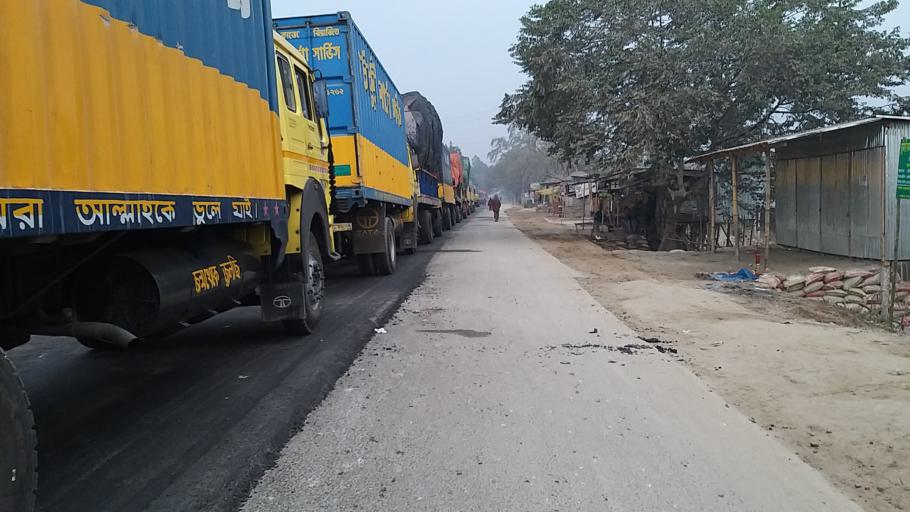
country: IN
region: West Bengal
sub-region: Koch Bihar
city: Haldibari
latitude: 26.4038
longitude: 88.9259
